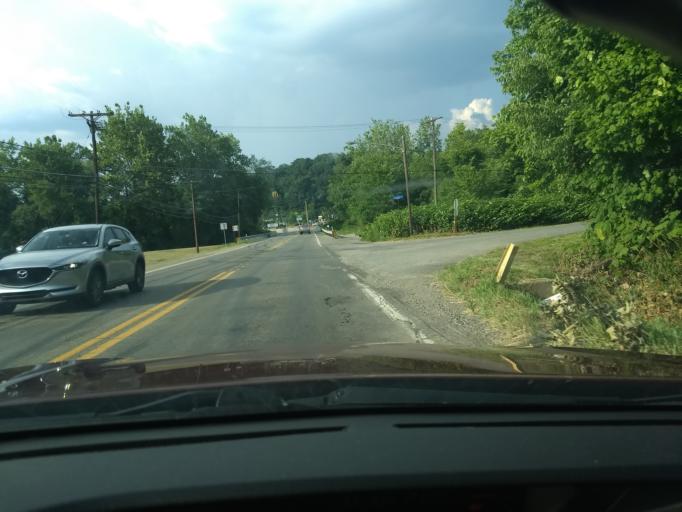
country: US
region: Pennsylvania
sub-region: Westmoreland County
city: Lower Burrell
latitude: 40.5493
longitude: -79.7588
